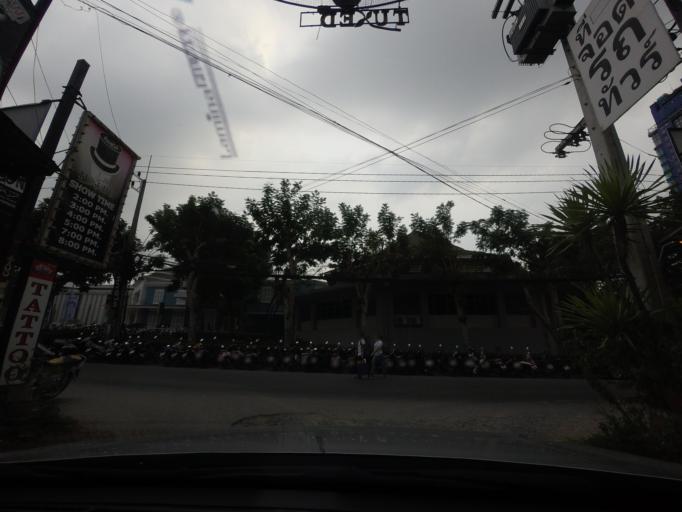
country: TH
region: Chon Buri
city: Phatthaya
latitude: 12.9466
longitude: 100.8898
